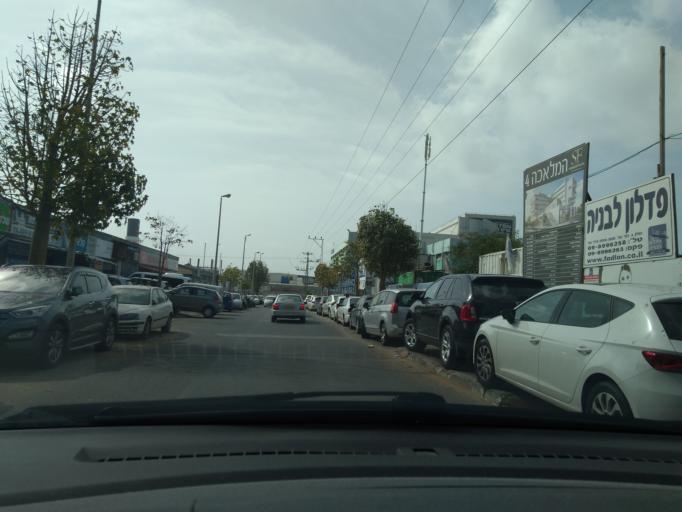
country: IL
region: Central District
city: Even Yehuda
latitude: 32.2773
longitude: 34.8582
